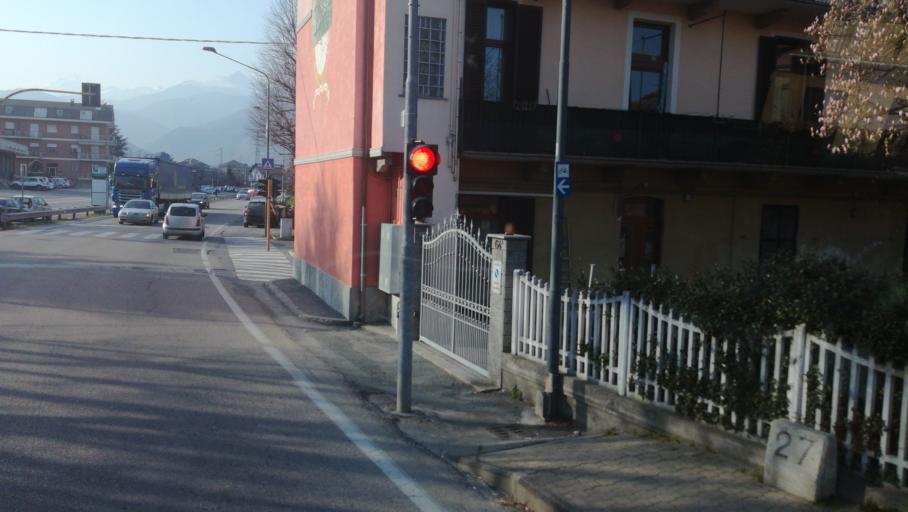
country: IT
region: Piedmont
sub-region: Provincia di Torino
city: Sant'Ambrogio di Torino
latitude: 45.1005
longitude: 7.3607
